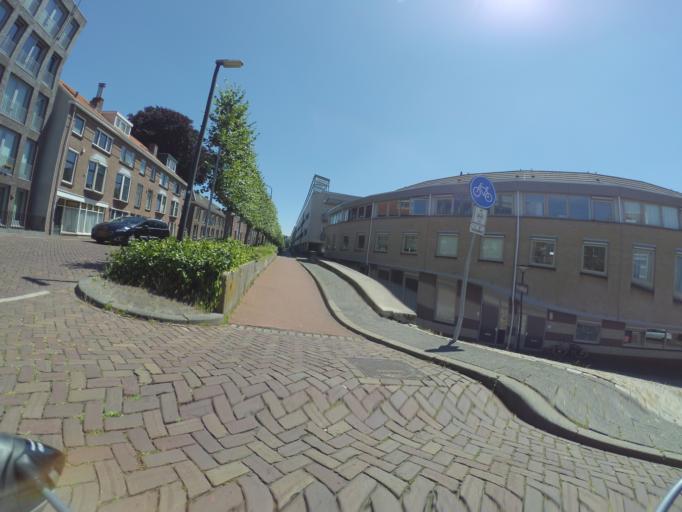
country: NL
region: South Holland
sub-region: Gemeente Dordrecht
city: Dordrecht
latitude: 51.8162
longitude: 4.6756
